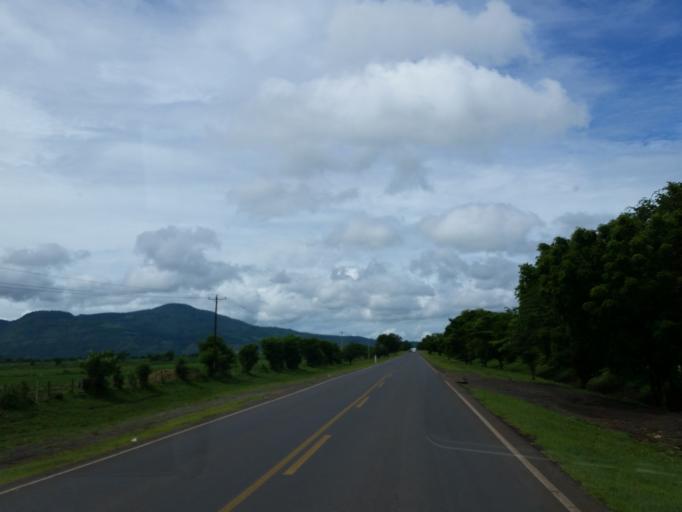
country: NI
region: Leon
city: Larreynaga
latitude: 12.6024
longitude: -86.6832
